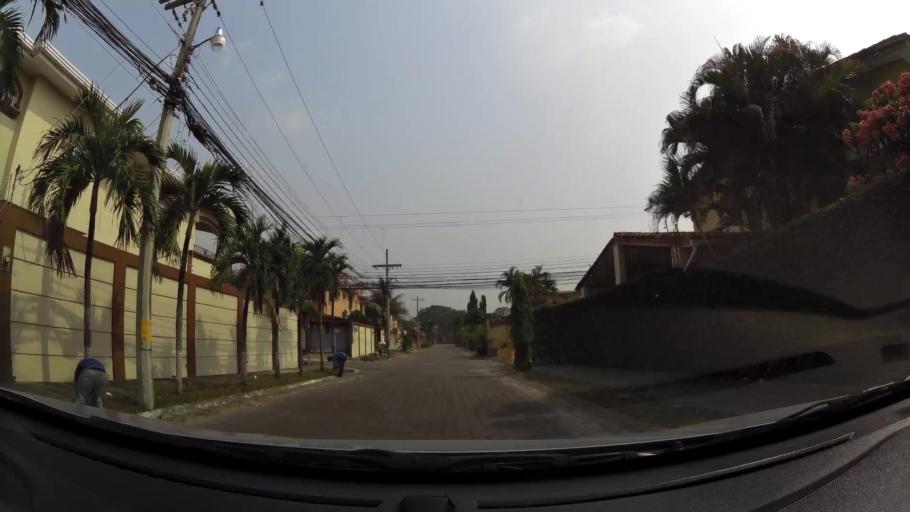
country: HN
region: Cortes
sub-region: San Pedro Sula
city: Pena Blanca
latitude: 15.5358
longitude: -88.0310
